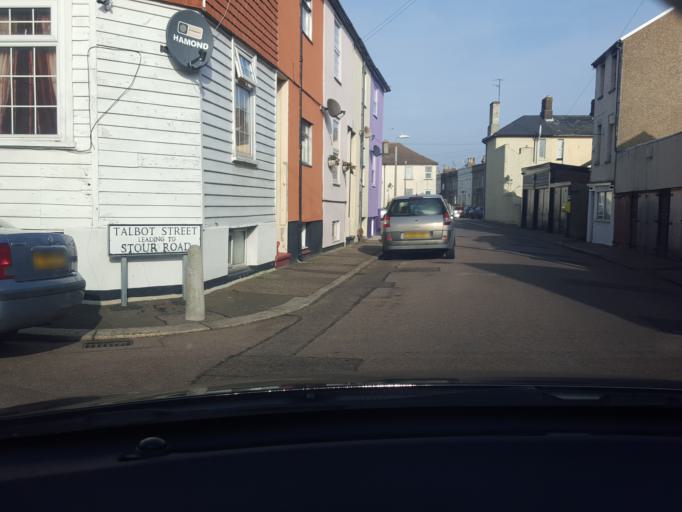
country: GB
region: England
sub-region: Essex
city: Harwich
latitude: 51.9409
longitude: 1.2839
